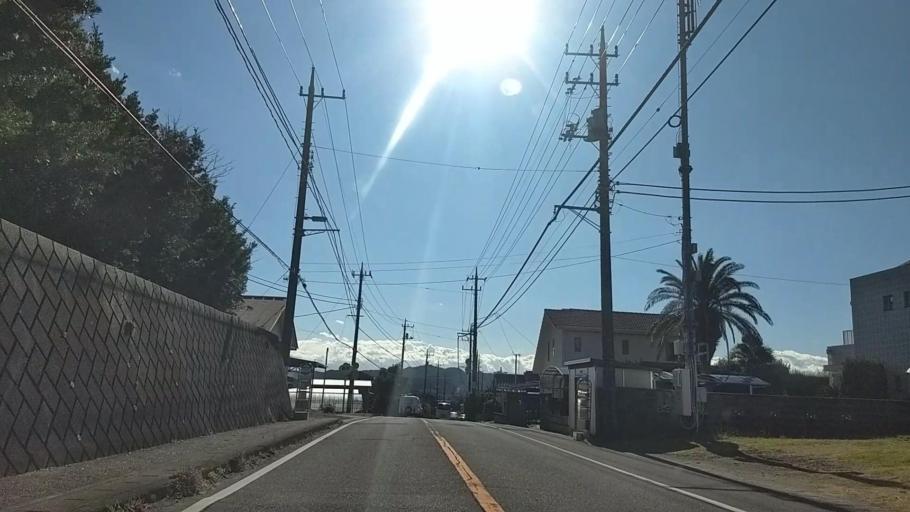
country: JP
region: Chiba
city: Tateyama
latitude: 34.9458
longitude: 139.8362
